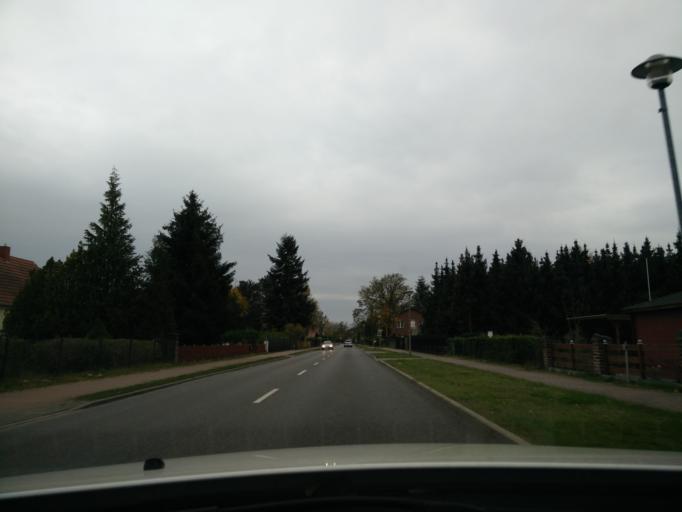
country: DE
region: Brandenburg
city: Velten
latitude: 52.6548
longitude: 13.1446
